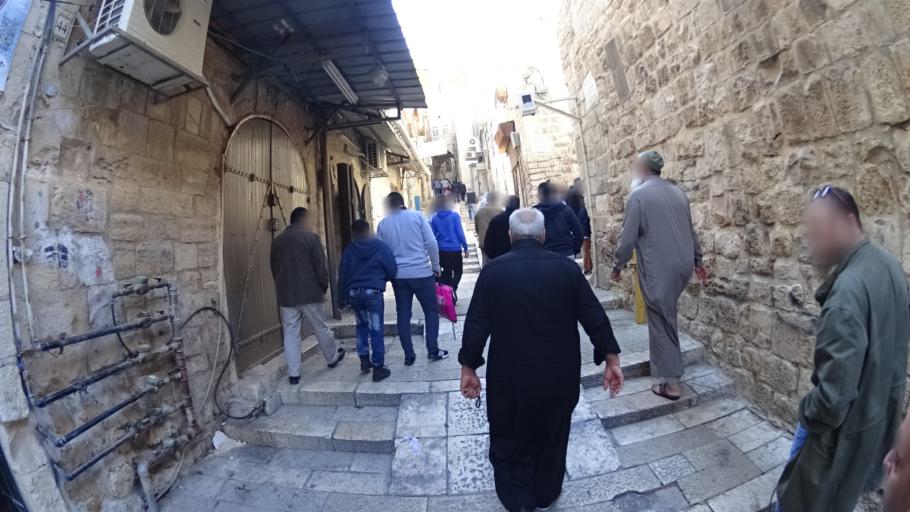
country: PS
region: West Bank
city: Old City
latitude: 31.7777
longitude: 35.2329
